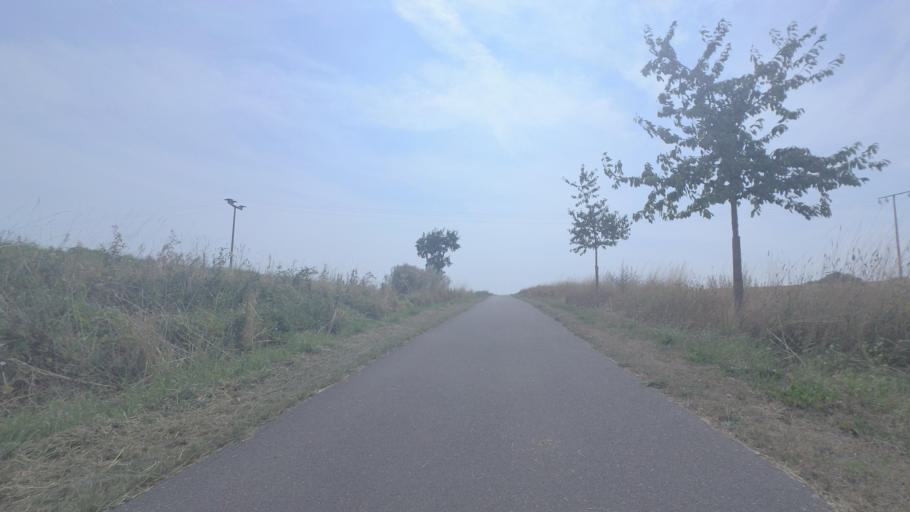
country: DE
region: Mecklenburg-Vorpommern
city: Garz
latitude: 54.3031
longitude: 13.3511
